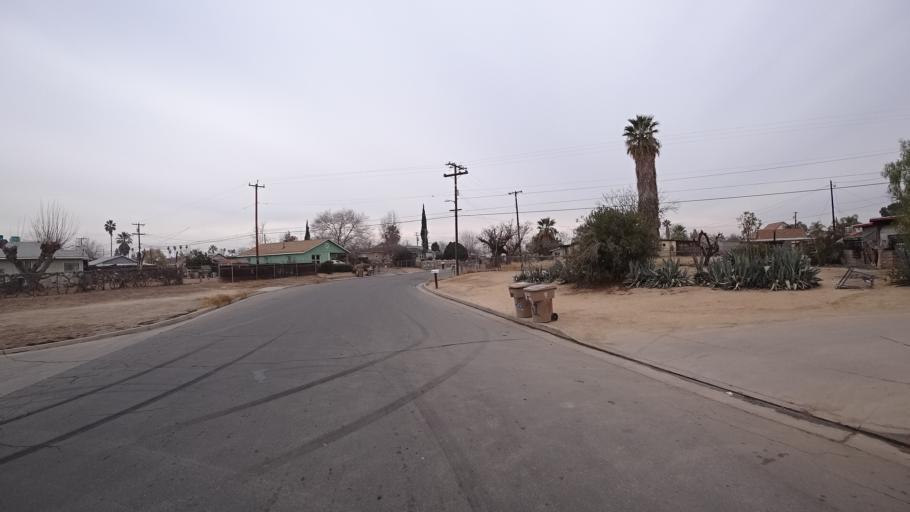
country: US
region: California
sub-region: Kern County
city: Bakersfield
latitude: 35.3645
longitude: -118.9991
